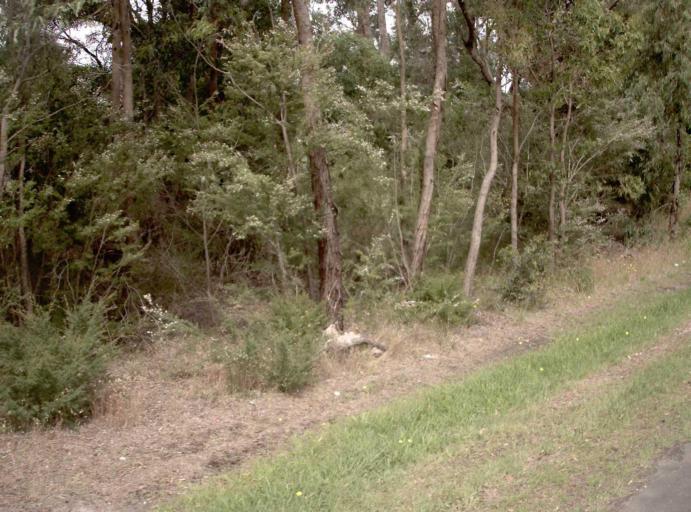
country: AU
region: Victoria
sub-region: Latrobe
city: Moe
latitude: -38.0847
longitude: 146.1977
